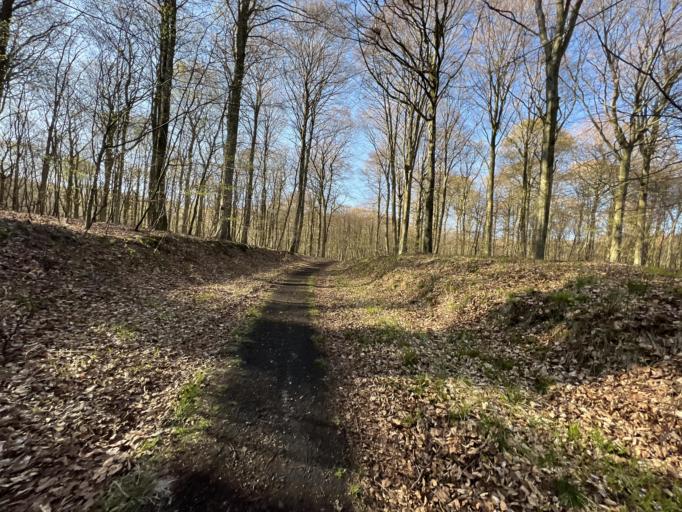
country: DE
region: Mecklenburg-Vorpommern
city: Sassnitz
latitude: 54.5345
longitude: 13.6396
